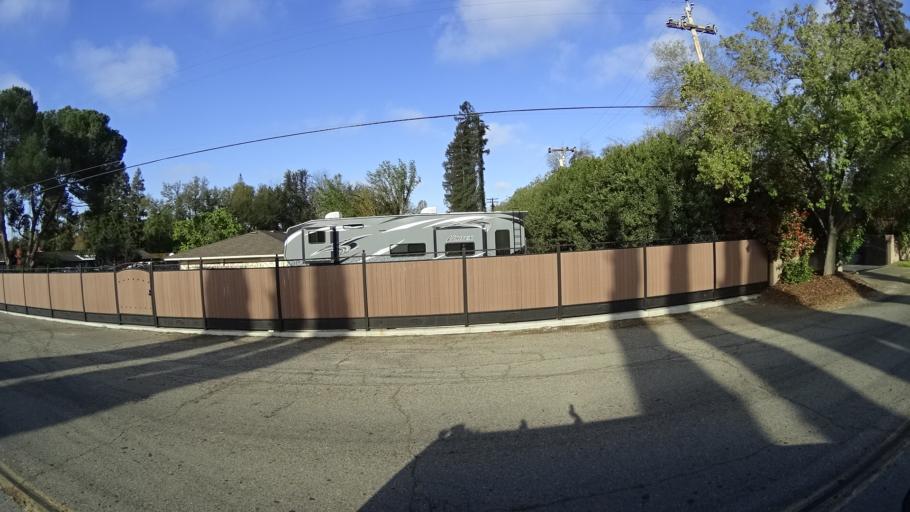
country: US
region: California
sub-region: Fresno County
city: Fresno
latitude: 36.8110
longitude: -119.8308
